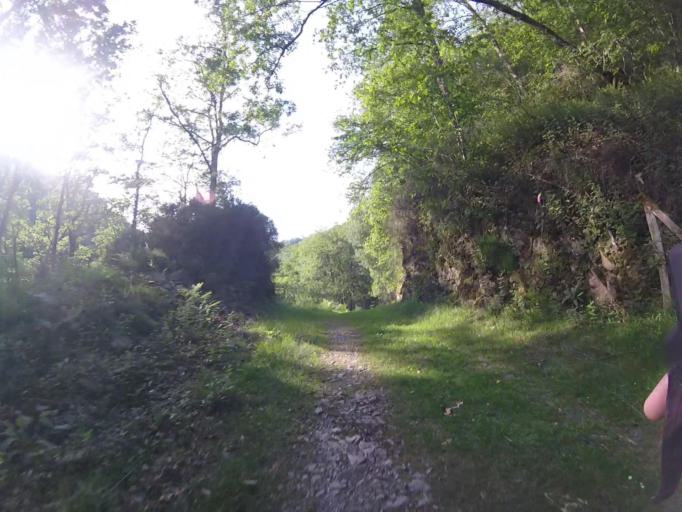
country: ES
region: Navarre
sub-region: Provincia de Navarra
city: Arano
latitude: 43.2379
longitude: -1.8704
